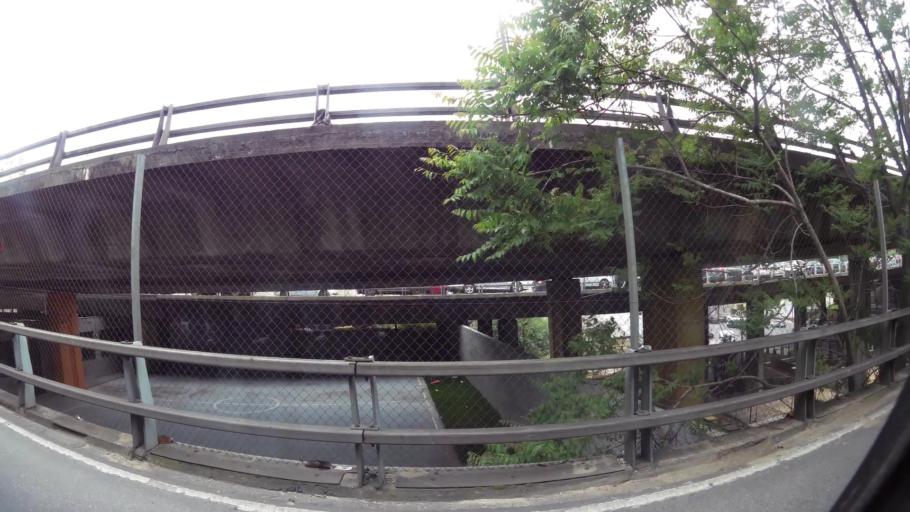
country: AR
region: Buenos Aires F.D.
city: Buenos Aires
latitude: -34.6227
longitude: -58.3689
